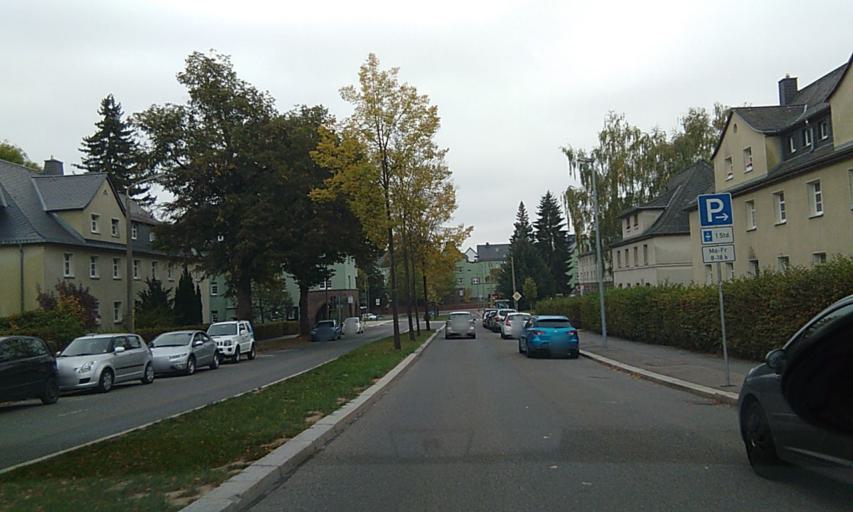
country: DE
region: Saxony
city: Chemnitz
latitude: 50.8404
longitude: 12.8874
